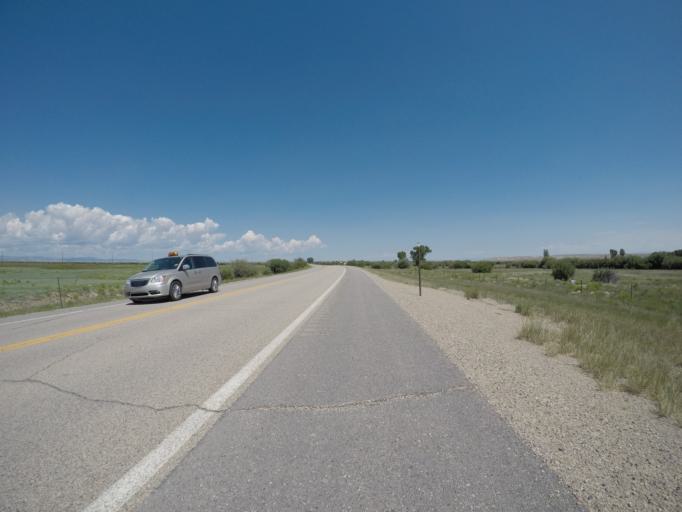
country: US
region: Wyoming
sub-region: Sublette County
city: Marbleton
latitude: 42.5175
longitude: -110.1051
